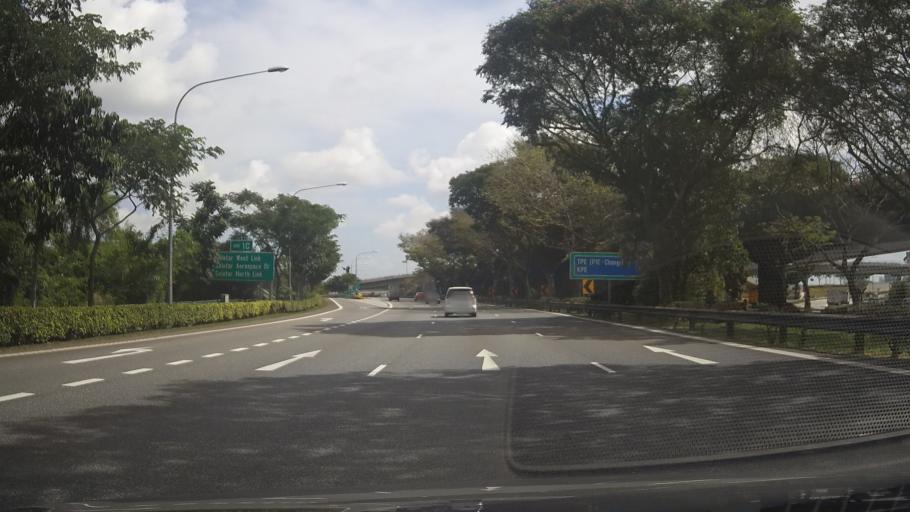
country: MY
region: Johor
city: Kampung Pasir Gudang Baru
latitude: 1.3978
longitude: 103.8534
